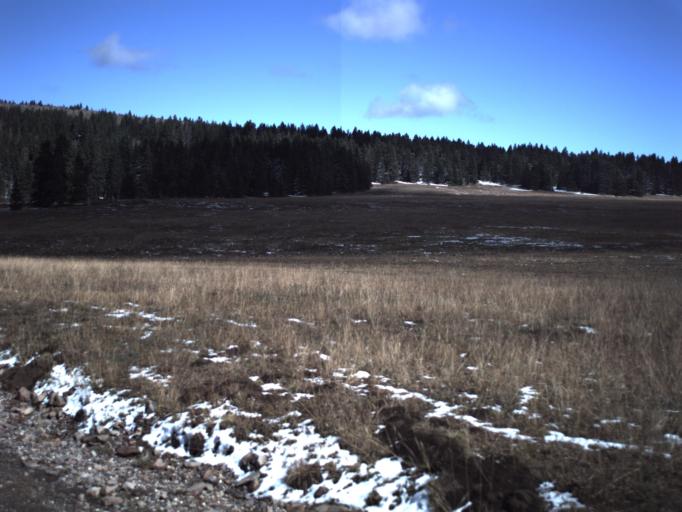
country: US
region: Utah
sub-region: Piute County
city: Junction
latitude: 38.2823
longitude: -112.3597
